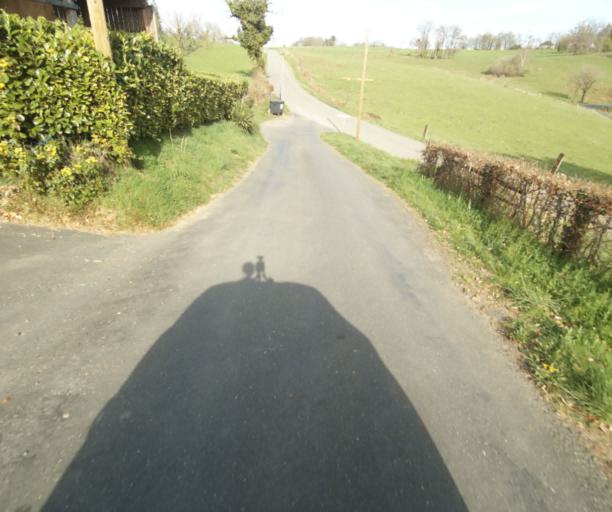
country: FR
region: Limousin
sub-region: Departement de la Correze
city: Naves
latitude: 45.3002
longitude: 1.7316
